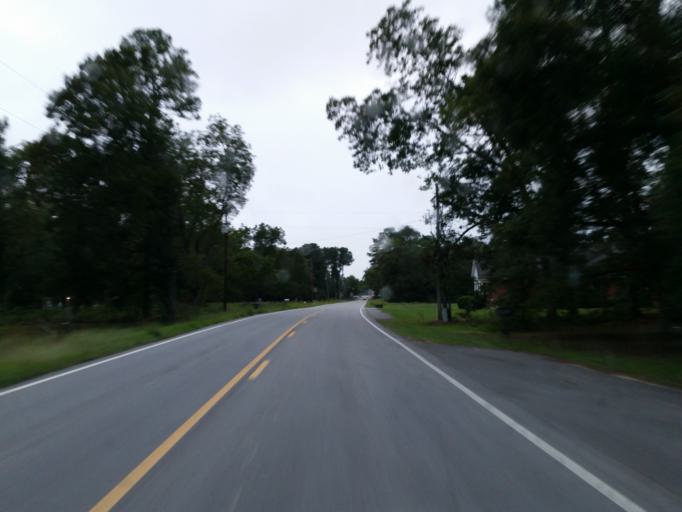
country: US
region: Georgia
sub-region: Crisp County
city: Cordele
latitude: 31.9019
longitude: -83.7620
